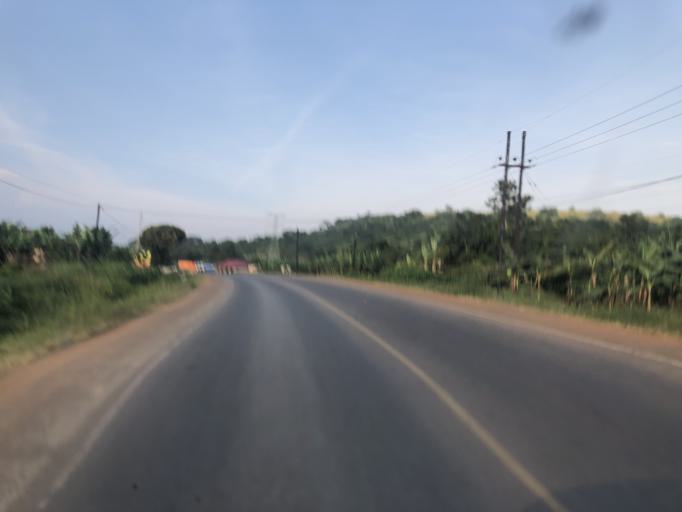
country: UG
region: Central Region
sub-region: Mpigi District
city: Mpigi
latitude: 0.1733
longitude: 32.2724
